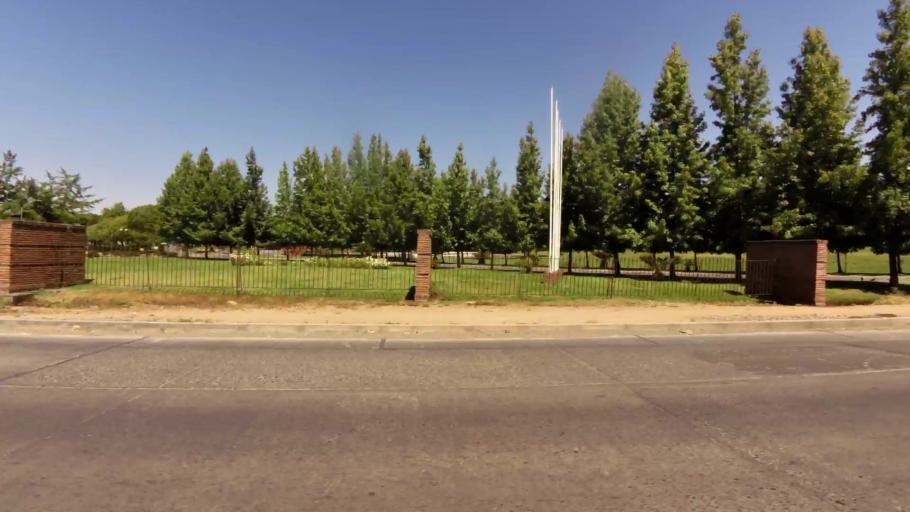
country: CL
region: Maule
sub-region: Provincia de Talca
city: Talca
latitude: -35.4020
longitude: -71.6356
